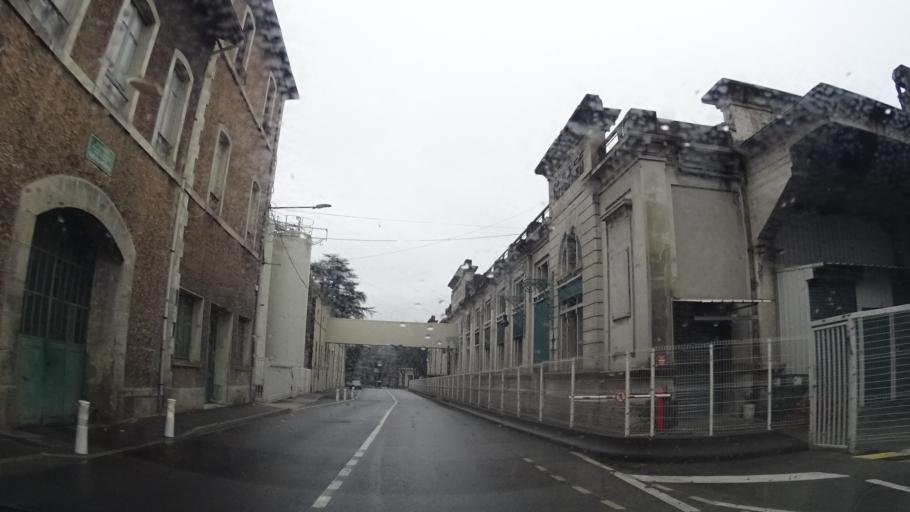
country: FR
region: Rhone-Alpes
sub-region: Departement de l'Ardeche
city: Vals-les-Bains
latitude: 44.6610
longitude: 4.3683
